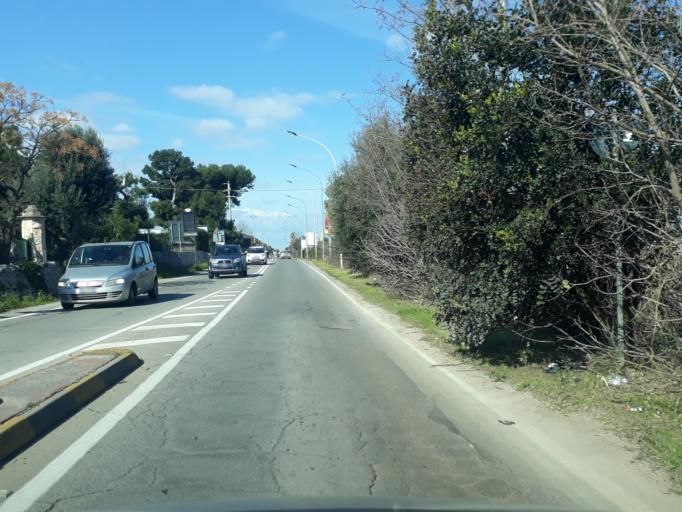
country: IT
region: Apulia
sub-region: Provincia di Bari
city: Monopoli
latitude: 40.9623
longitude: 17.2802
